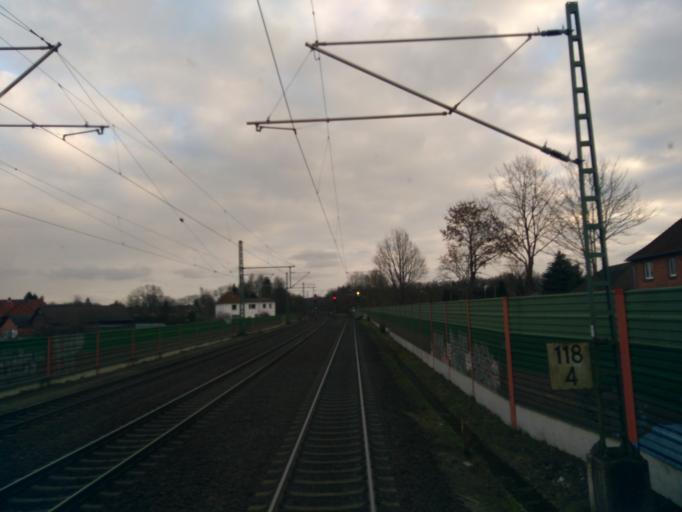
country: DE
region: Lower Saxony
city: Bienenbuttel
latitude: 53.1406
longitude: 10.4866
